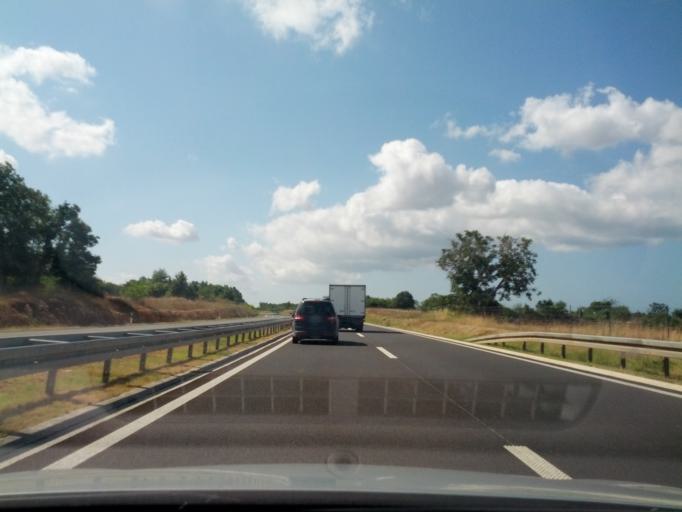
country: HR
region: Istarska
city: Vodnjan
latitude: 45.0030
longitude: 13.8373
